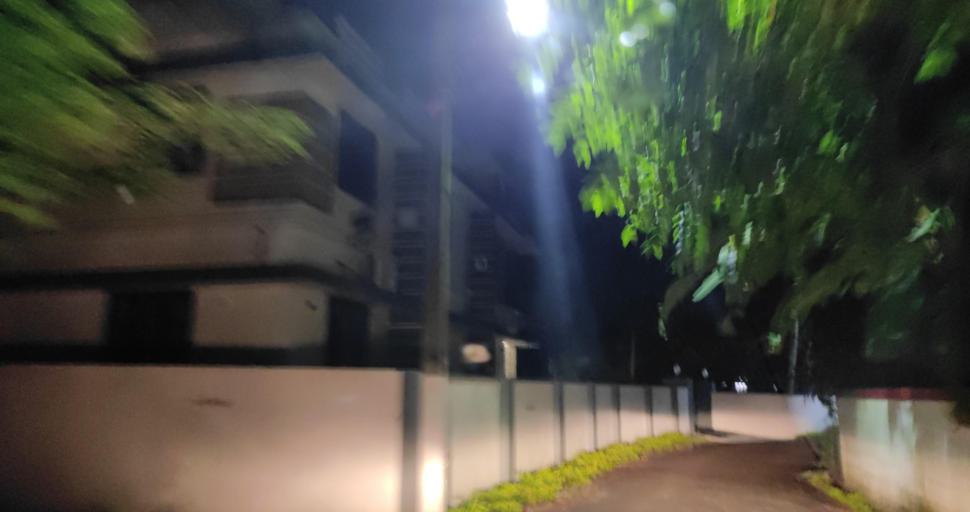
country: IN
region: Kerala
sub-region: Alappuzha
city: Shertallai
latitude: 9.6177
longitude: 76.3340
